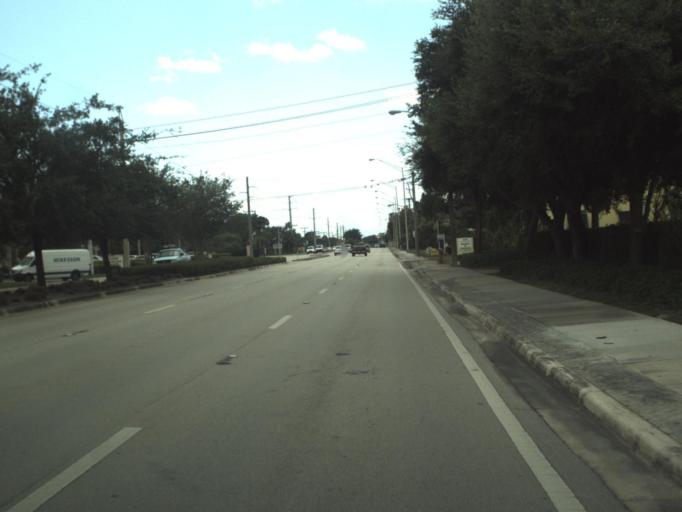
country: US
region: Florida
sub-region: Martin County
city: Stuart
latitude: 27.1838
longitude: -80.2532
